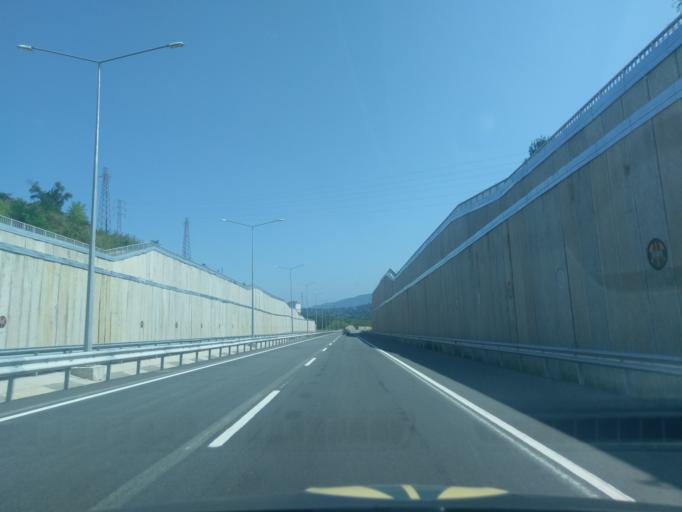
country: TR
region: Ordu
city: Ordu
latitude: 40.9563
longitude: 37.8834
